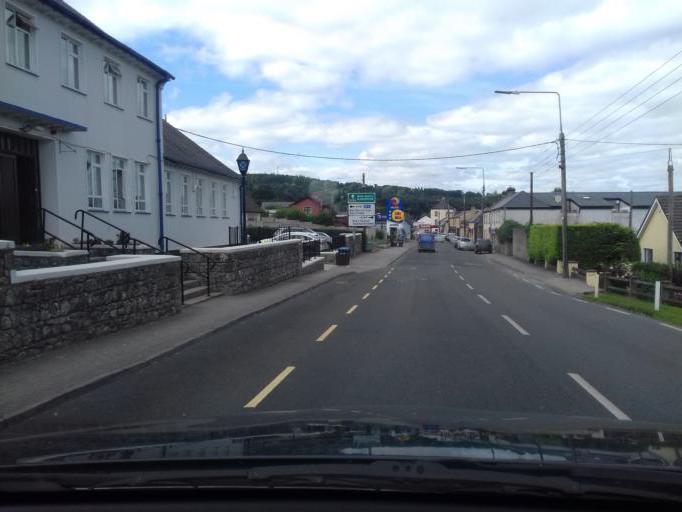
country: IE
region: Leinster
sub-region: Wicklow
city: Baltinglass
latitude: 52.9389
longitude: -6.7095
